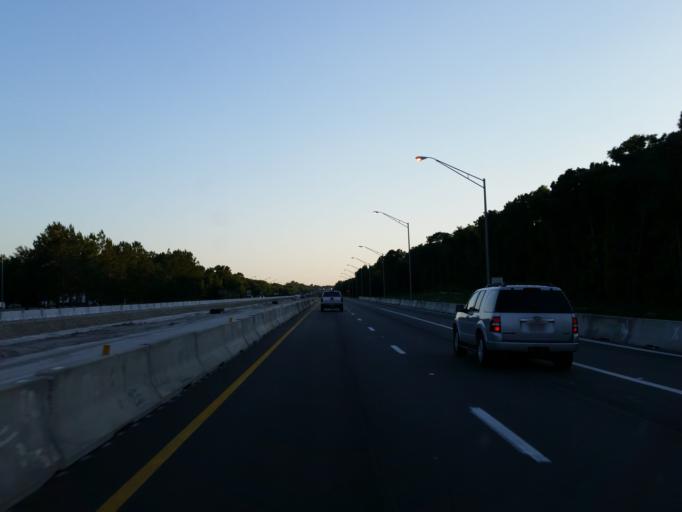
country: US
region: Florida
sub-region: Hernando County
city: Ridge Manor
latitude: 28.5861
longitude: -82.2120
